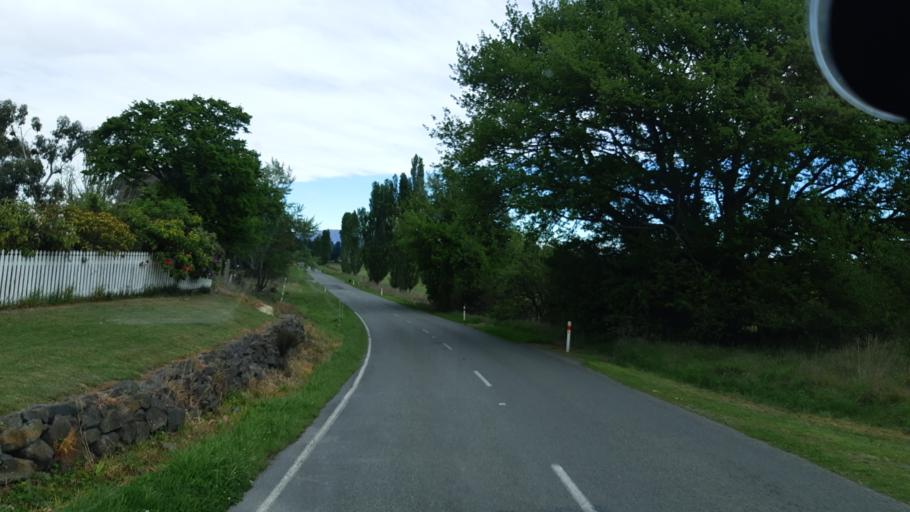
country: NZ
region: Canterbury
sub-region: Timaru District
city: Timaru
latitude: -44.4380
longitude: 171.1772
